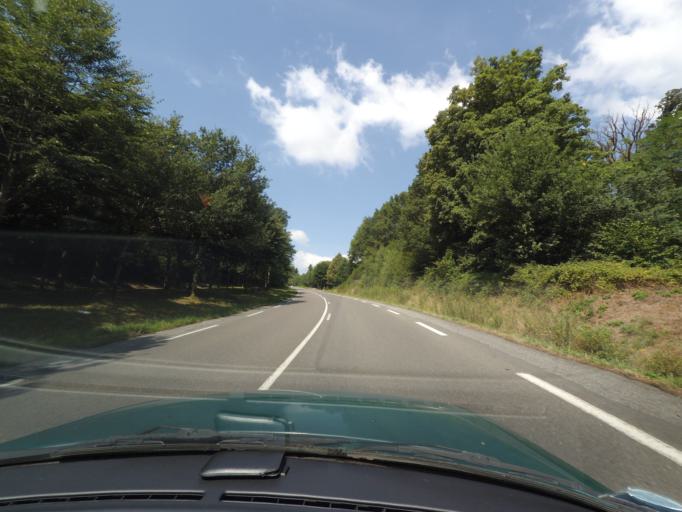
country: FR
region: Limousin
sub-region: Departement de la Haute-Vienne
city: Eymoutiers
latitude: 45.7390
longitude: 1.7312
